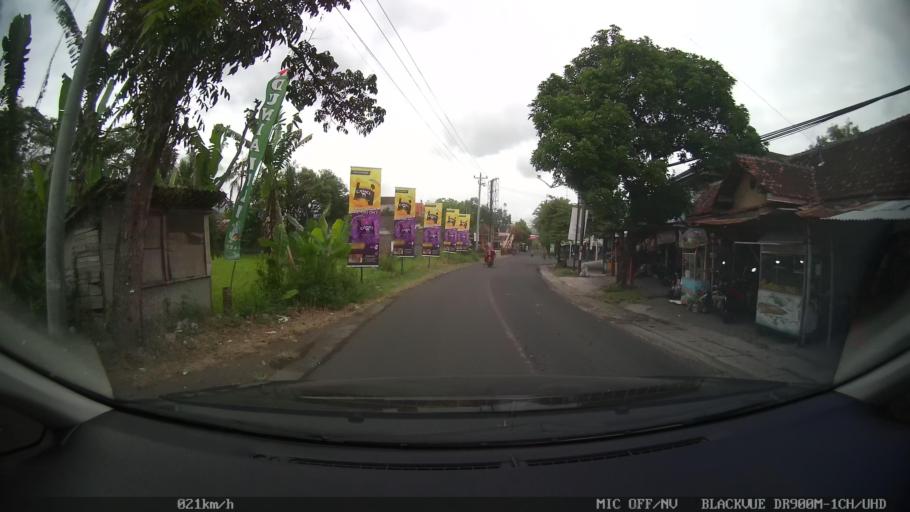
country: ID
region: Daerah Istimewa Yogyakarta
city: Sewon
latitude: -7.8672
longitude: 110.4077
